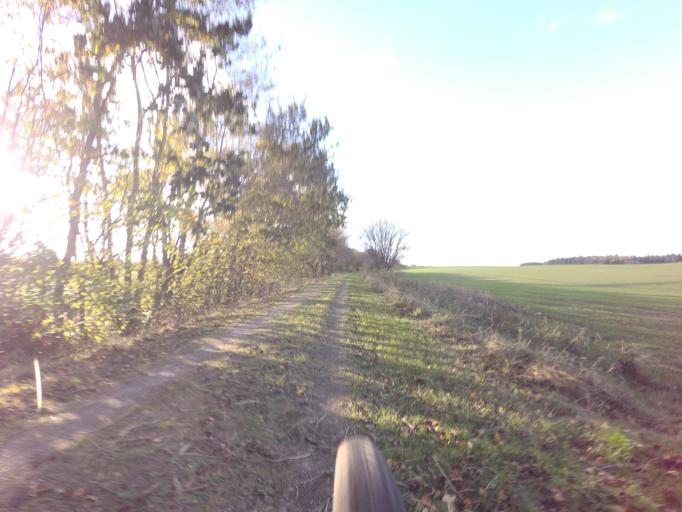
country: DK
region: Central Jutland
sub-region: Syddjurs Kommune
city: Ryomgard
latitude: 56.4907
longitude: 10.6798
